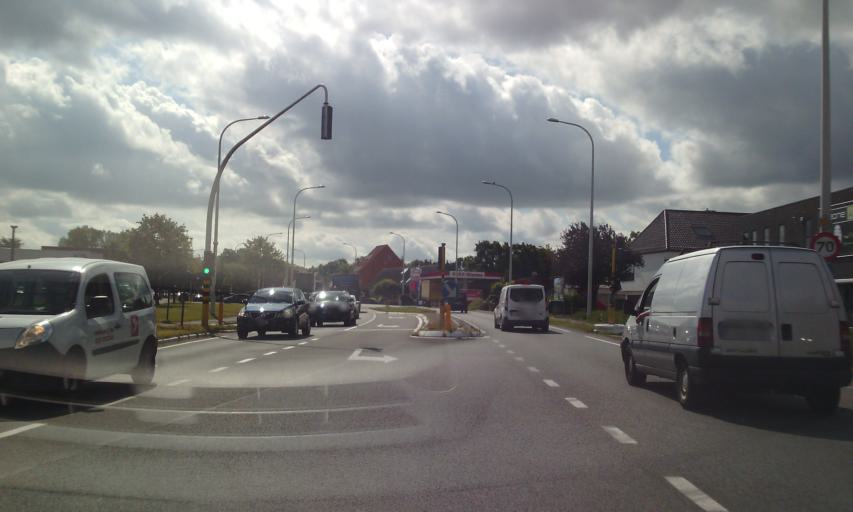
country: BE
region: Flanders
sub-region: Provincie Oost-Vlaanderen
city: Lokeren
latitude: 51.1119
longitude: 3.9608
